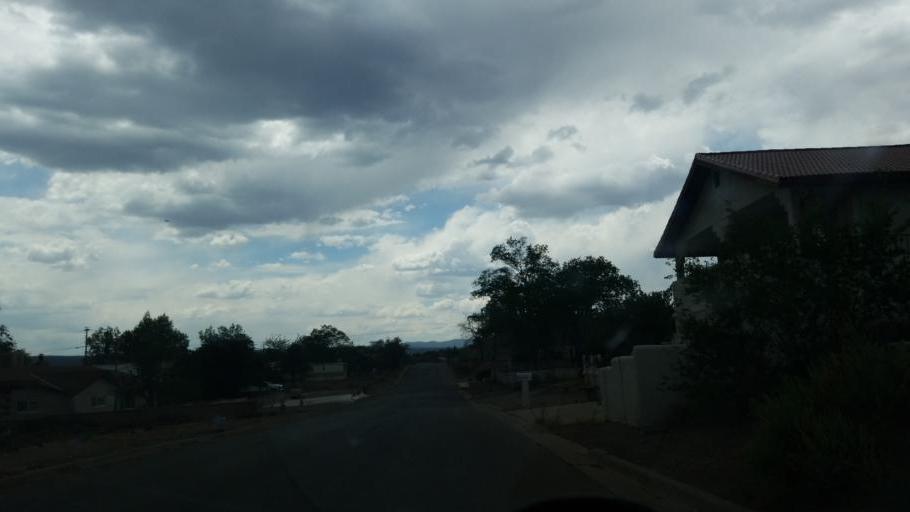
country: US
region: New Mexico
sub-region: Cibola County
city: Grants
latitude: 35.1573
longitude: -107.8551
